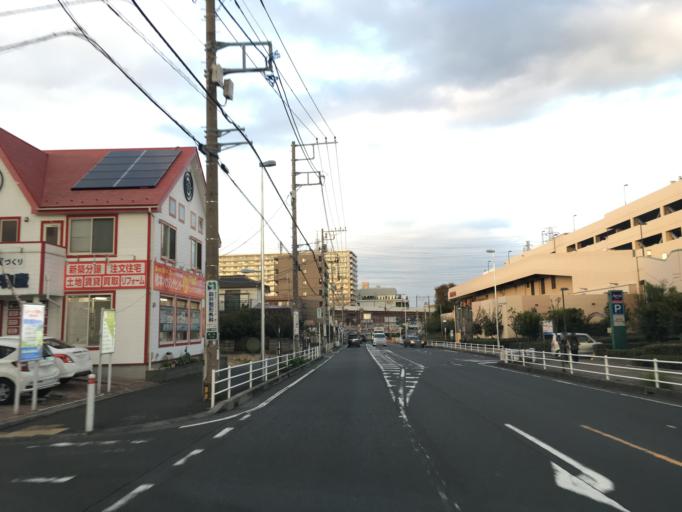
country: JP
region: Tokyo
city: Hachioji
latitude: 35.5909
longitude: 139.3471
